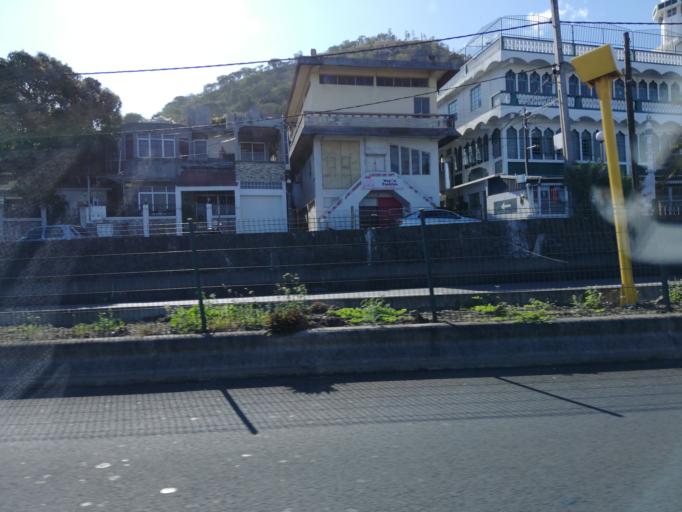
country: MU
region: Moka
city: Pailles
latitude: -20.1806
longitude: 57.4810
